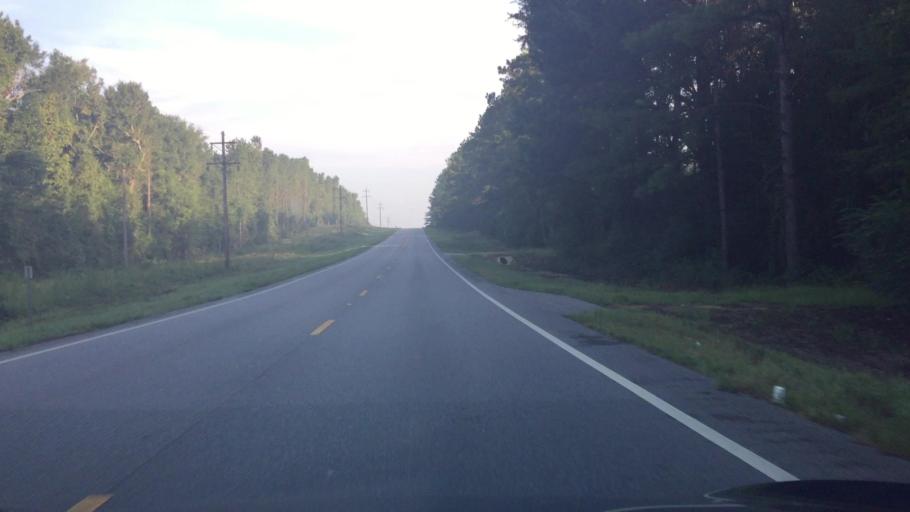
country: US
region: Alabama
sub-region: Covington County
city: Florala
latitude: 31.0607
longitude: -86.3947
